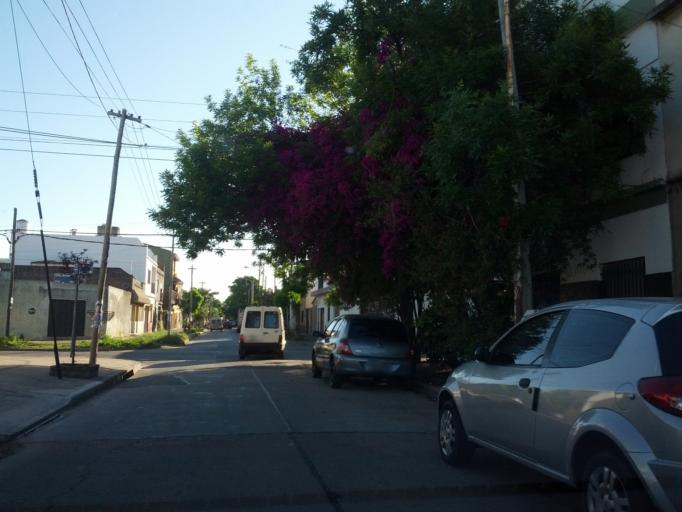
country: AR
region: Buenos Aires
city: San Justo
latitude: -34.6625
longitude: -58.5339
